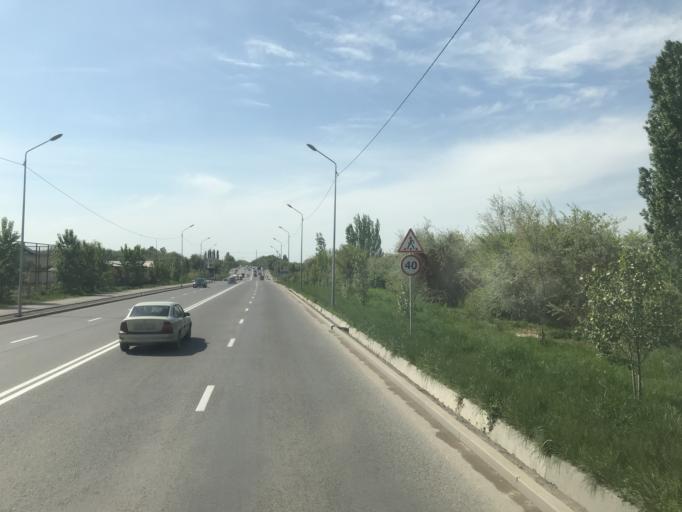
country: KZ
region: Almaty Oblysy
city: Burunday
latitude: 43.3094
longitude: 76.8718
